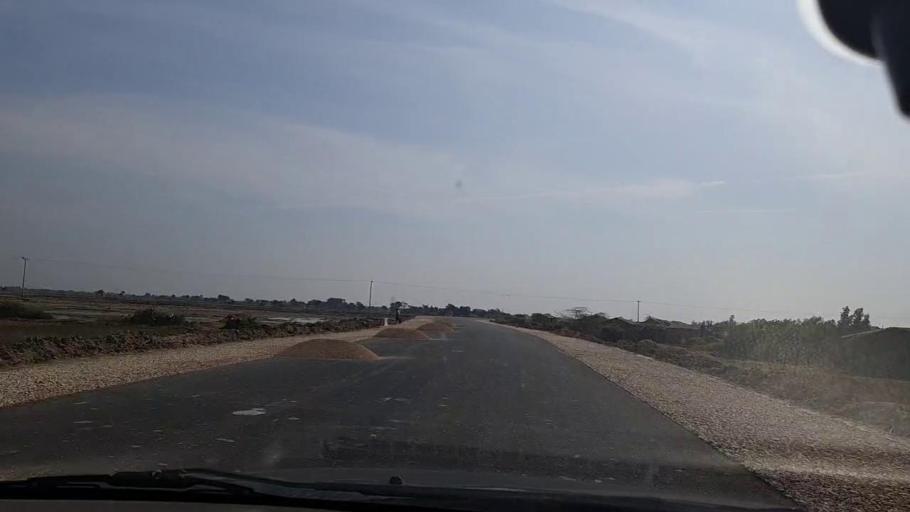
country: PK
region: Sindh
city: Mirpur Batoro
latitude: 24.7457
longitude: 68.2730
